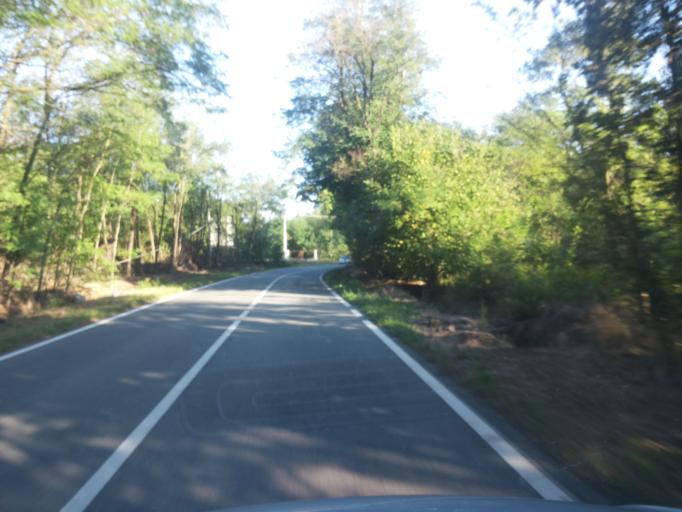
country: IT
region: Piedmont
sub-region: Provincia di Vercelli
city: Borgo d'Ale
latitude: 45.3654
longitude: 8.0359
